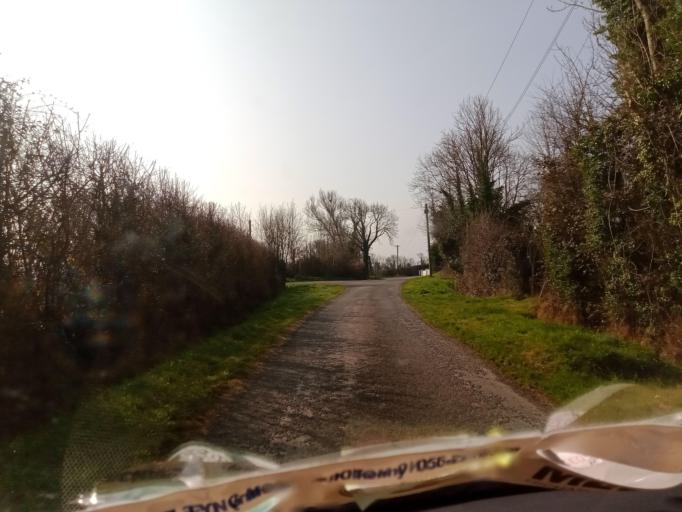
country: IE
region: Leinster
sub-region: Kilkenny
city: Callan
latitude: 52.5235
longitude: -7.4008
